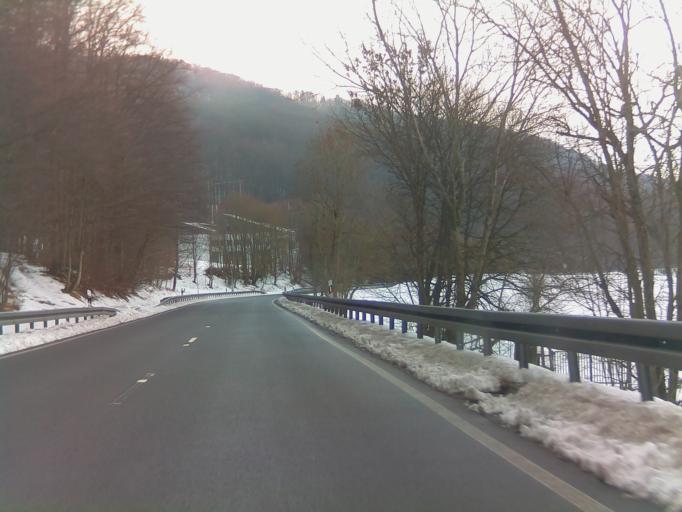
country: DE
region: Bavaria
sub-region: Regierungsbezirk Unterfranken
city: Sandberg
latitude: 50.3496
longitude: 9.9530
